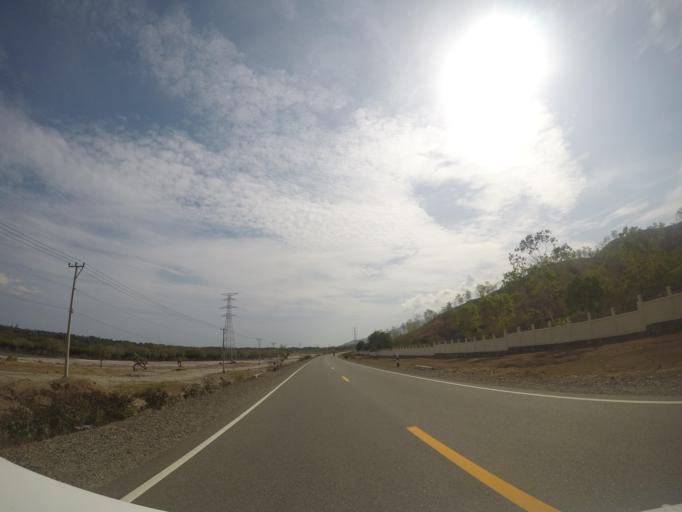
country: ID
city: Metinaro
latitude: -8.5126
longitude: 125.7840
